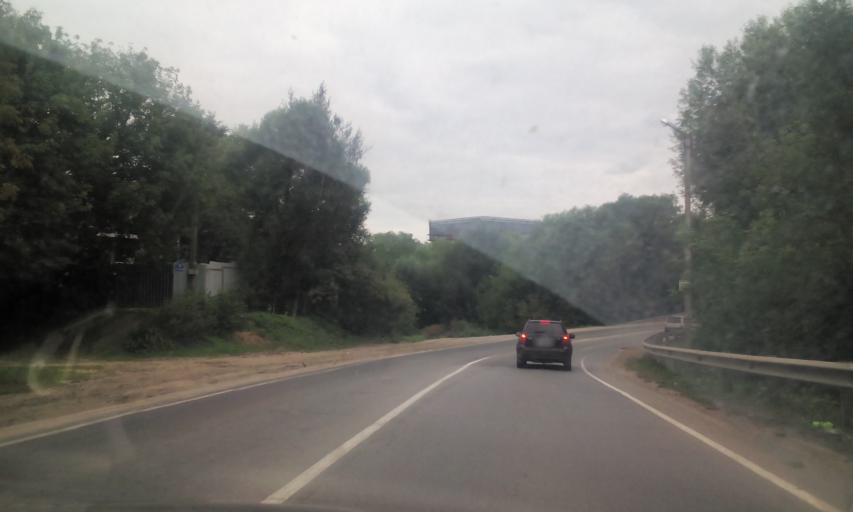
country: RU
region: Kaluga
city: Kaluga
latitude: 54.5151
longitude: 36.3451
